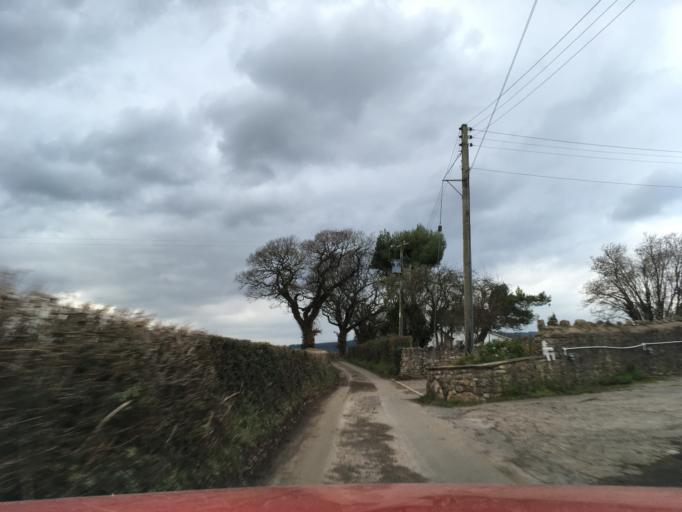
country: GB
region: Wales
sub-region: Newport
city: Llanvaches
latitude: 51.6125
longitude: -2.8089
